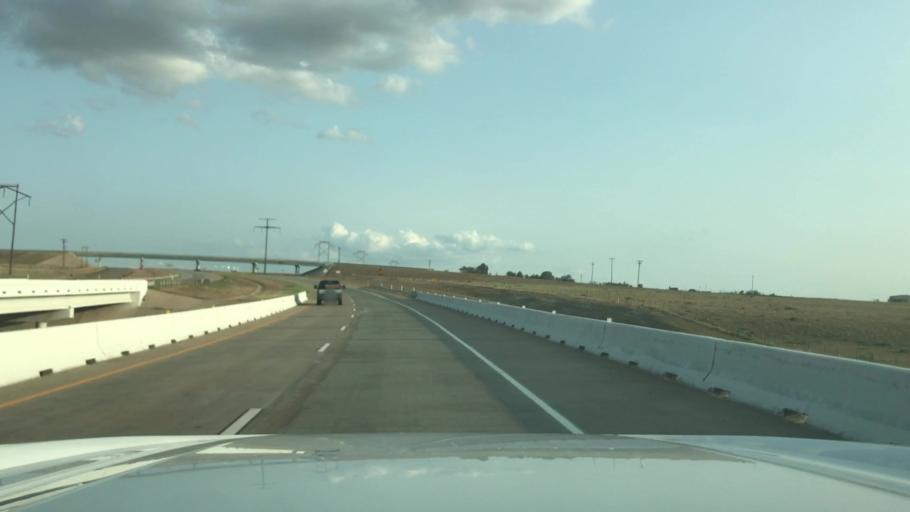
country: US
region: Texas
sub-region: Swisher County
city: Tulia
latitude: 34.5194
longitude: -101.7956
